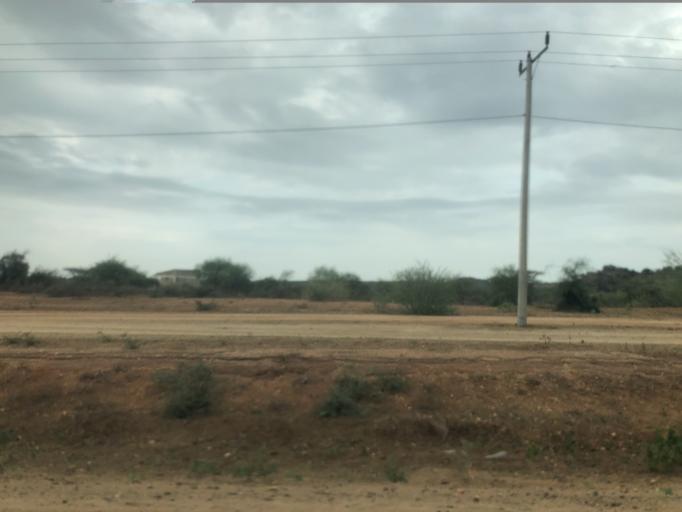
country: ET
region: Southern Nations, Nationalities, and People's Region
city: Turmi
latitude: 4.9740
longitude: 36.4851
